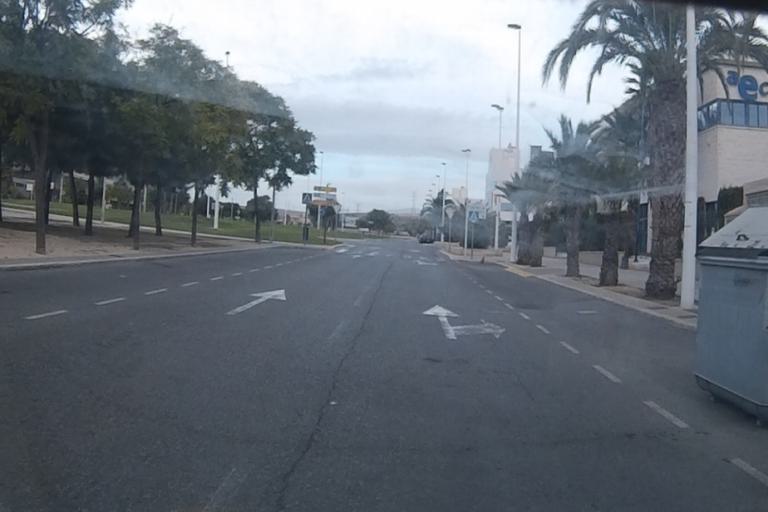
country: ES
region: Valencia
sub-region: Provincia de Alicante
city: Elche
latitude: 38.2925
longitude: -0.6109
